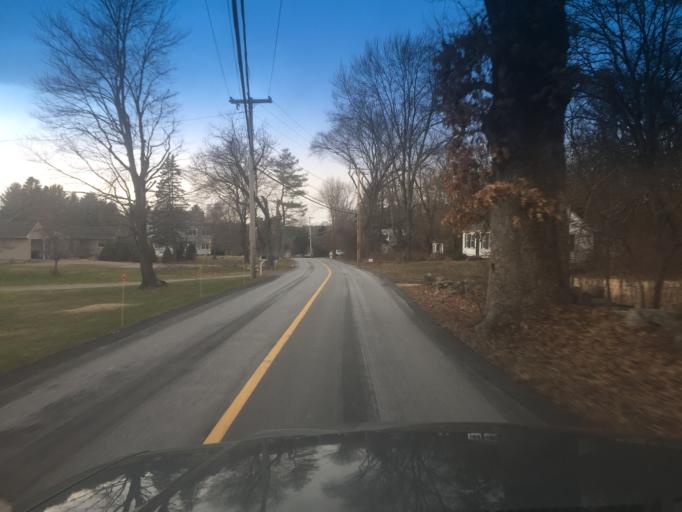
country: US
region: Massachusetts
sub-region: Norfolk County
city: Medway
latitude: 42.1265
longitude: -71.4033
